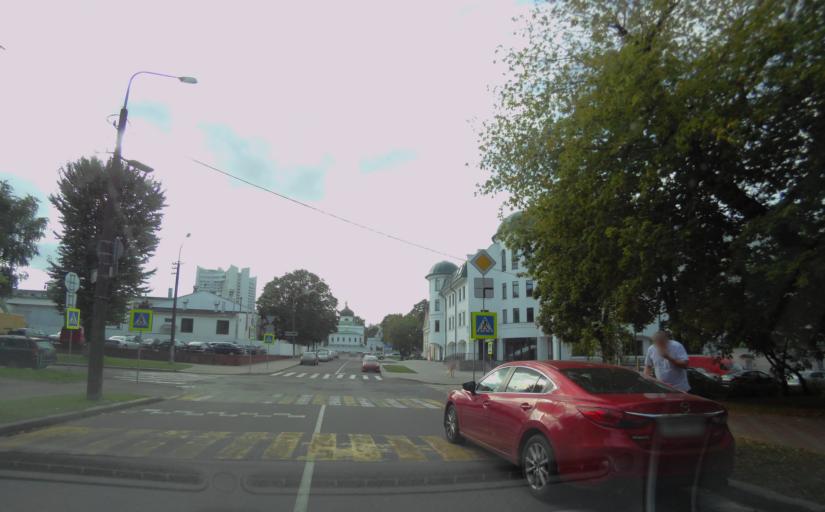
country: BY
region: Minsk
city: Minsk
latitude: 53.9158
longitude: 27.5567
